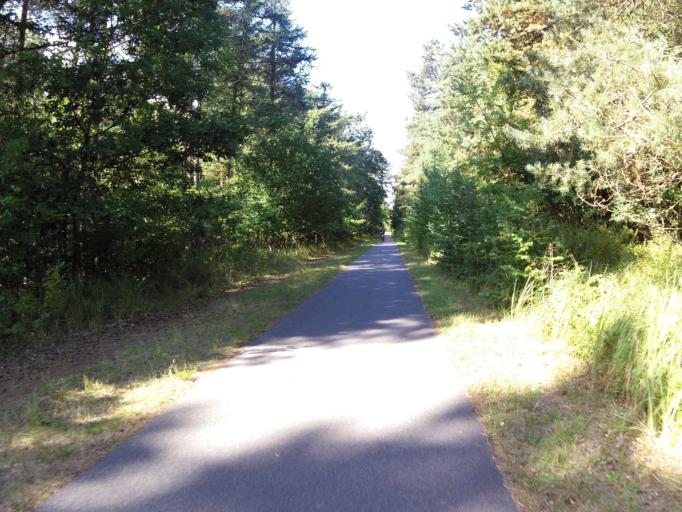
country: DE
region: Mecklenburg-Vorpommern
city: Karlshagen
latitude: 54.1429
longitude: 13.8118
